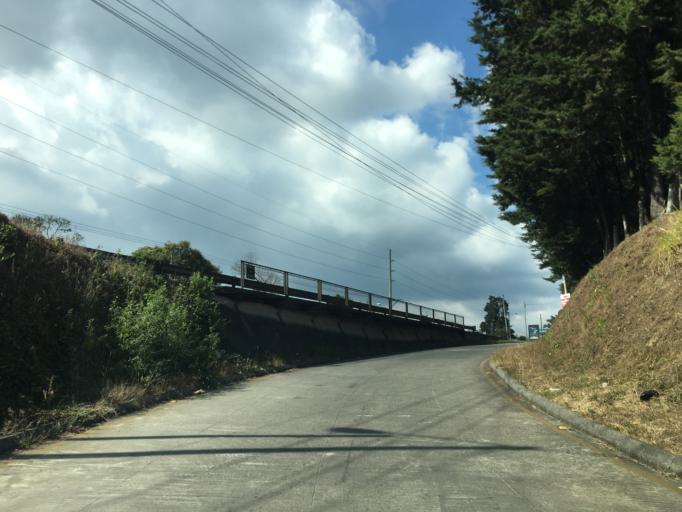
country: GT
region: Guatemala
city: Villa Canales
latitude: 14.4901
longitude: -90.4833
